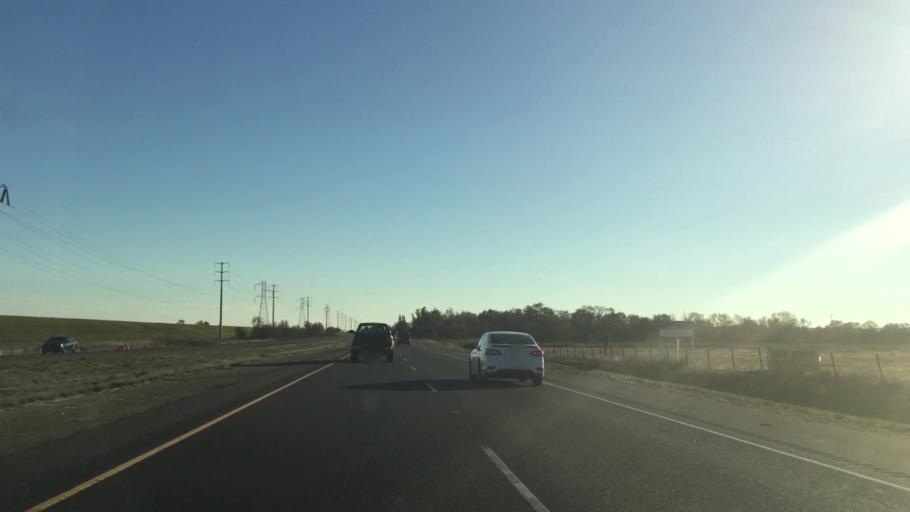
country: US
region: California
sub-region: Yuba County
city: Plumas Lake
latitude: 39.0511
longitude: -121.5433
